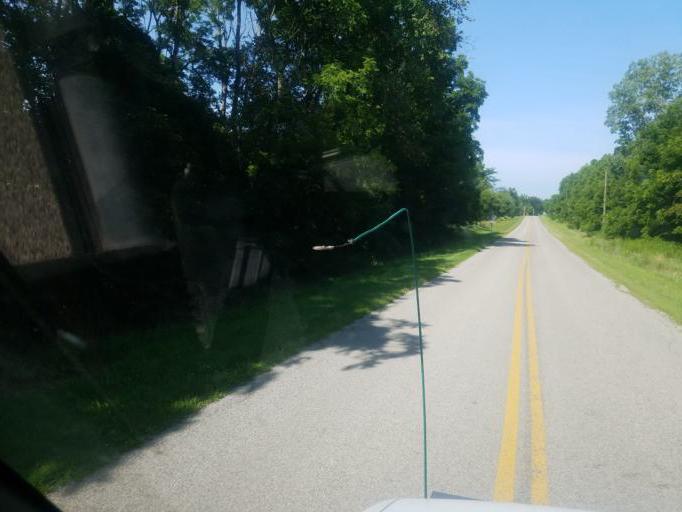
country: US
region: Ohio
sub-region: Union County
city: Marysville
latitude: 40.2826
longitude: -83.2656
